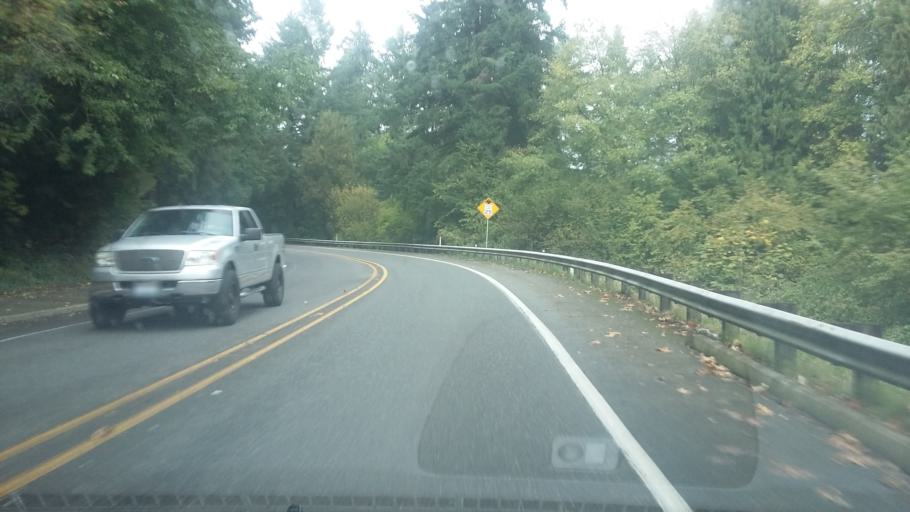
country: US
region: Washington
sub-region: Clark County
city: Ridgefield
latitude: 45.8156
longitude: -122.7341
